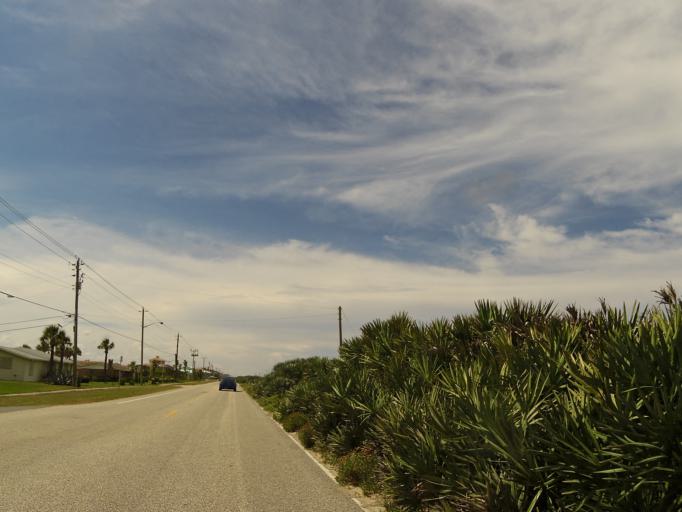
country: US
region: Florida
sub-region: Volusia County
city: Ormond-by-the-Sea
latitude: 29.3648
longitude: -81.0740
